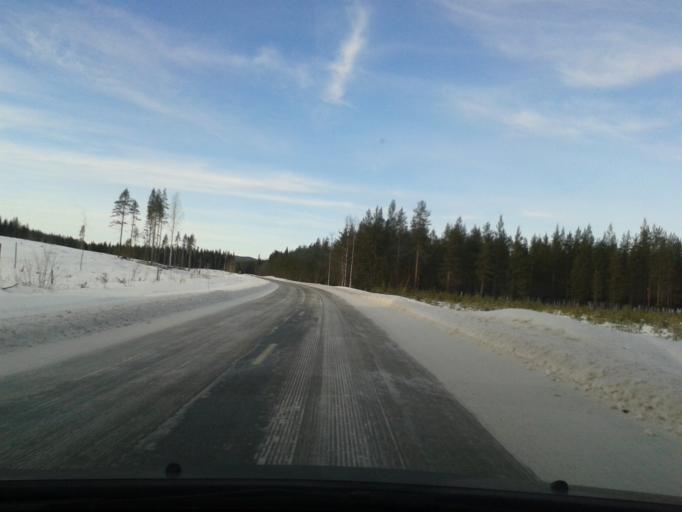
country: SE
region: Vaesternorrland
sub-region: OErnskoeldsviks Kommun
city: Bredbyn
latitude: 63.5950
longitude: 17.9179
